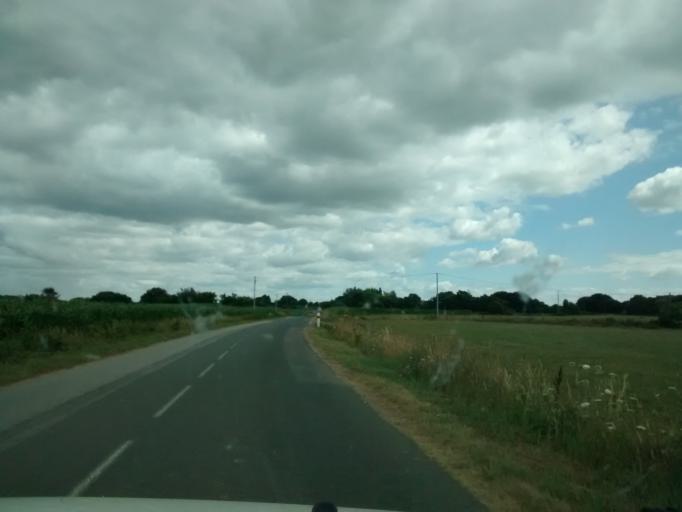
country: FR
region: Brittany
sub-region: Departement du Finistere
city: Lesneven
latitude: 48.5722
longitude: -4.2714
